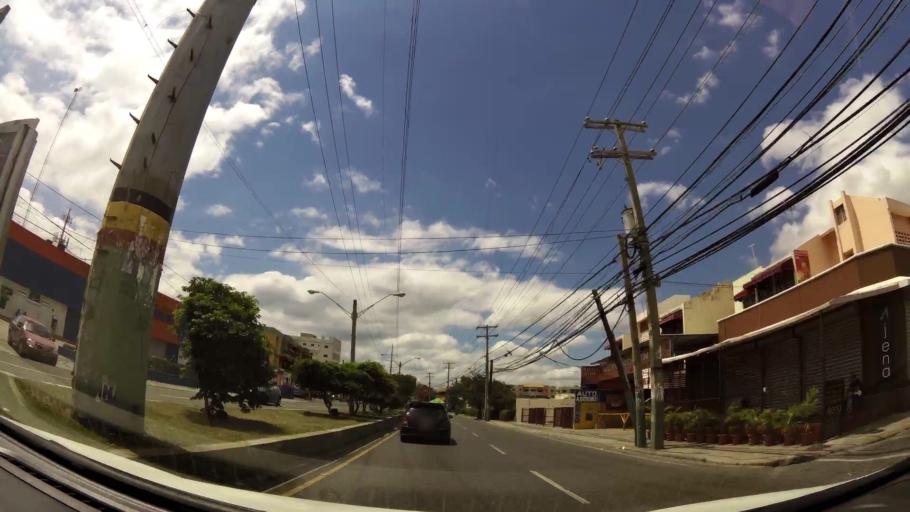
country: DO
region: Nacional
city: Bella Vista
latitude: 18.4377
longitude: -69.9540
